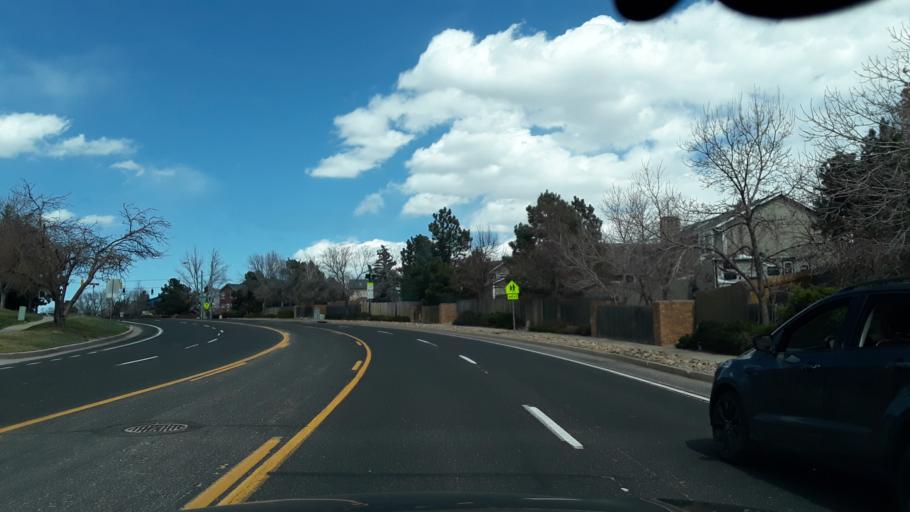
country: US
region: Colorado
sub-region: El Paso County
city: Black Forest
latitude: 38.9462
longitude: -104.7539
